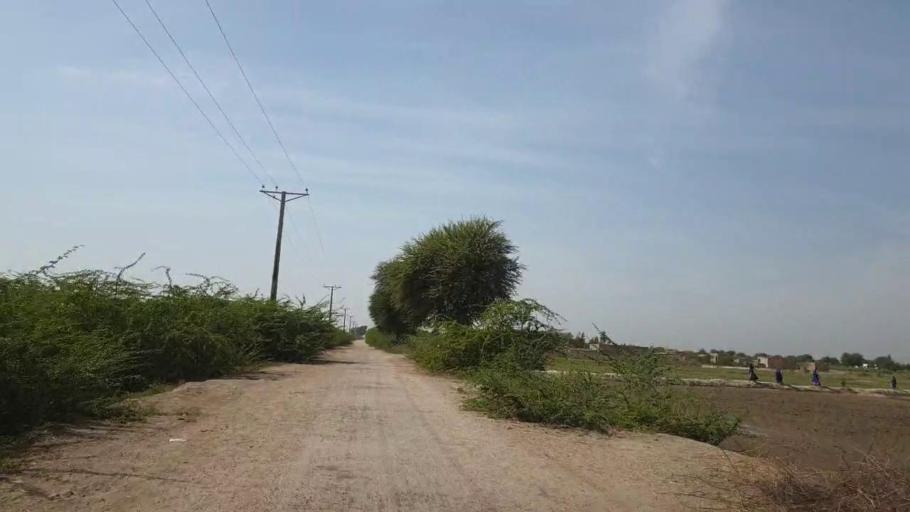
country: PK
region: Sindh
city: Kunri
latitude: 25.2065
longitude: 69.5465
